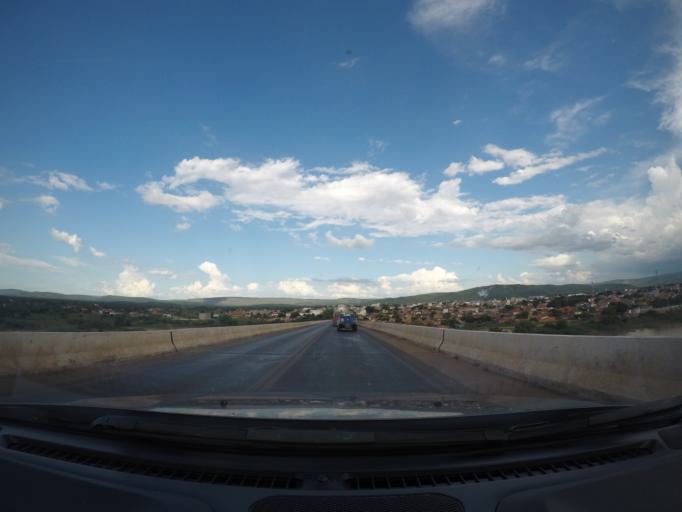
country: BR
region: Bahia
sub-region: Ibotirama
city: Ibotirama
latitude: -12.1802
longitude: -43.2260
